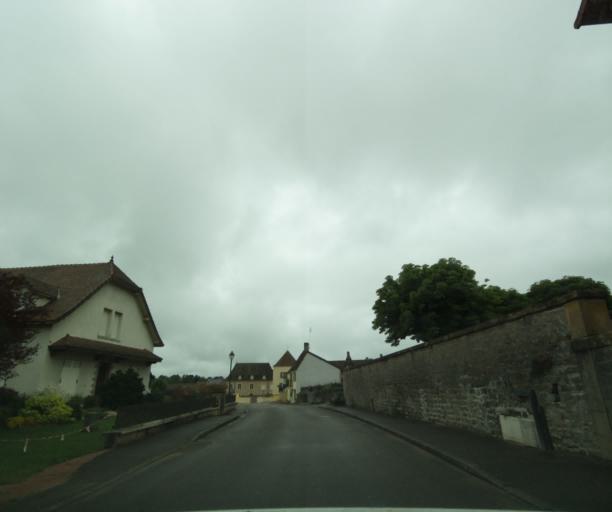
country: FR
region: Bourgogne
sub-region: Departement de Saone-et-Loire
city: Charolles
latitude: 46.4401
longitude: 4.3387
